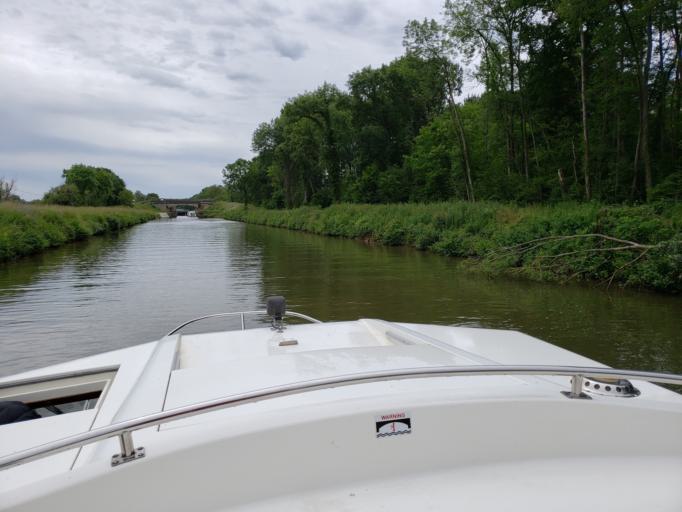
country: FR
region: Bourgogne
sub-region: Departement de l'Yonne
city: Appoigny
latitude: 47.8988
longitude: 3.5360
